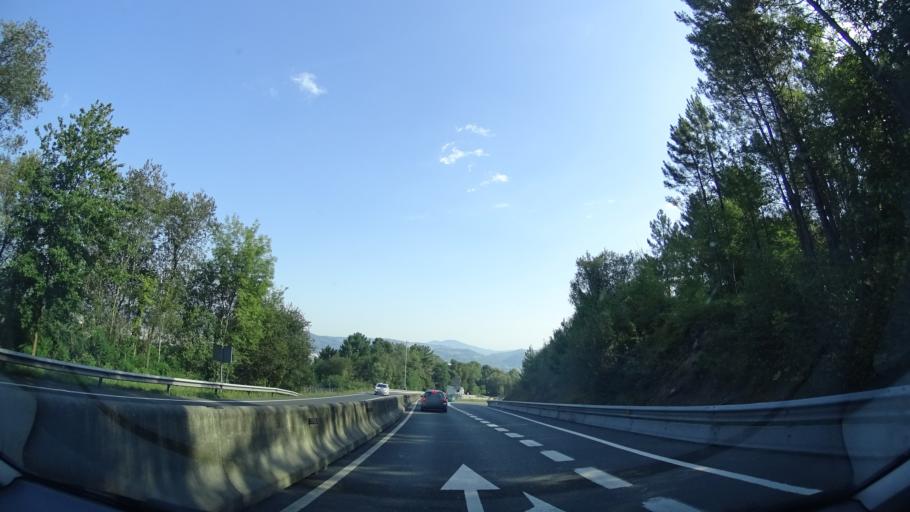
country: ES
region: Basque Country
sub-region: Bizkaia
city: Bilbao
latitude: 43.2790
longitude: -2.8999
